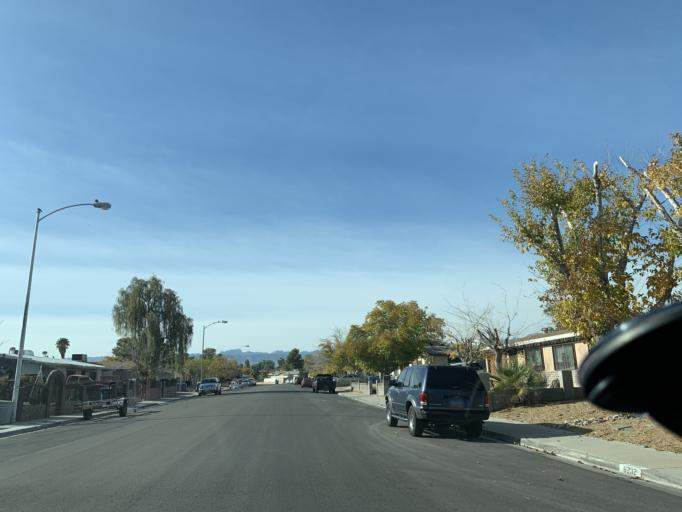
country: US
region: Nevada
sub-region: Clark County
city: Spring Valley
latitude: 36.1104
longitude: -115.2278
